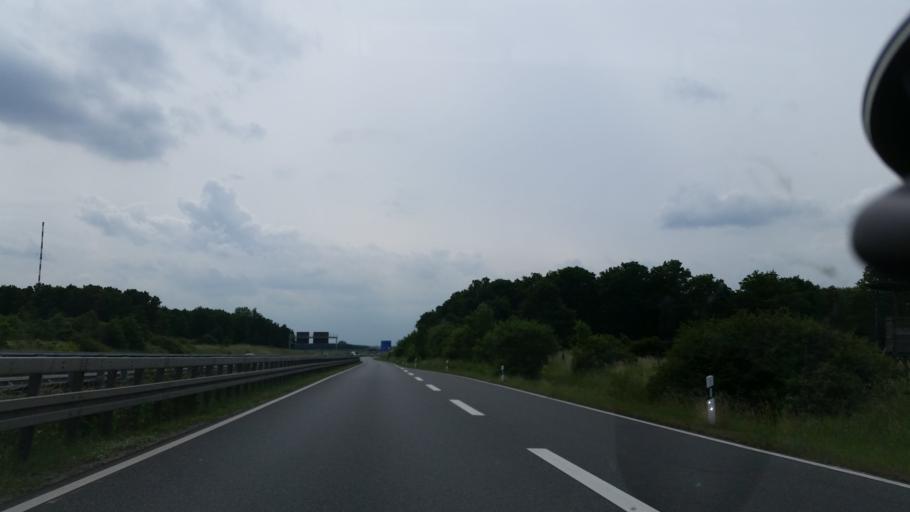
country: DE
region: Lower Saxony
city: Lehre
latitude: 52.3053
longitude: 10.7254
